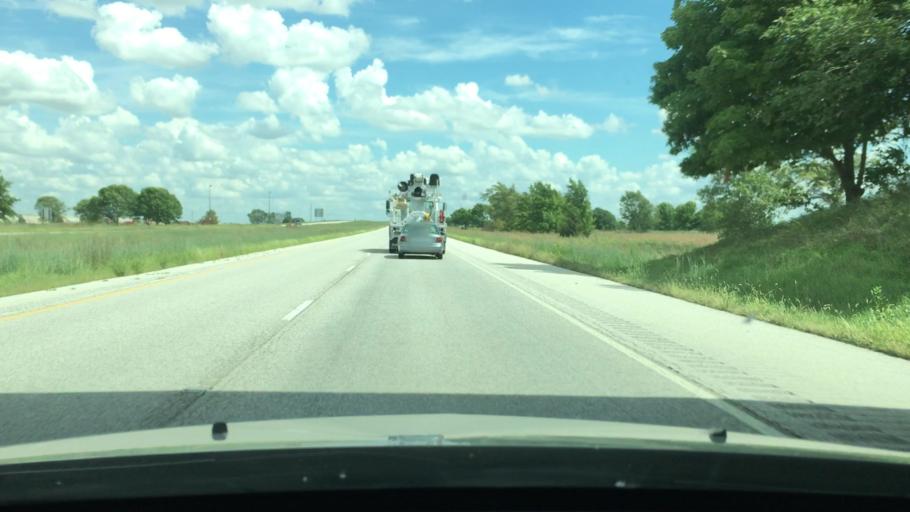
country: US
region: Illinois
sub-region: Morgan County
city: South Jacksonville
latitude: 39.6864
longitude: -90.2284
